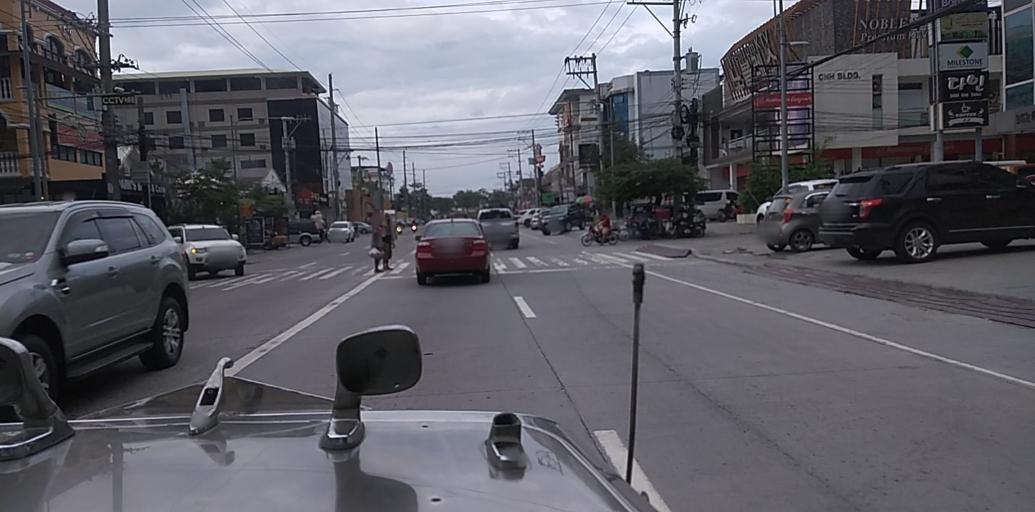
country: PH
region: Central Luzon
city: Santol
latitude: 15.1608
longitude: 120.5559
